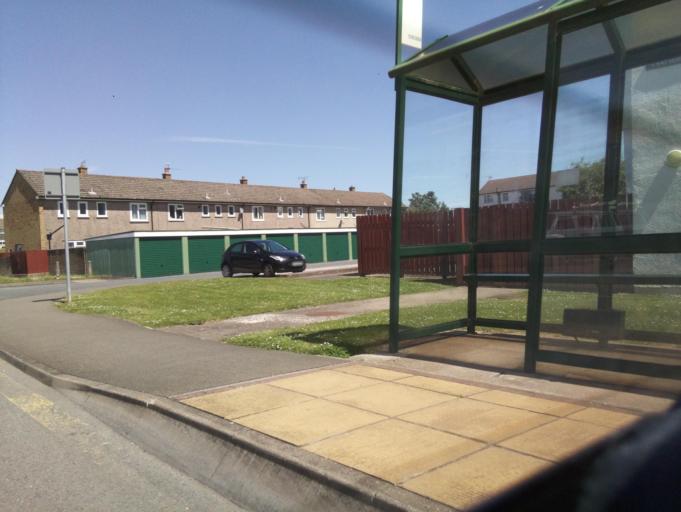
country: GB
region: Wales
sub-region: Monmouthshire
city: Caldicot
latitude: 51.5870
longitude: -2.7634
